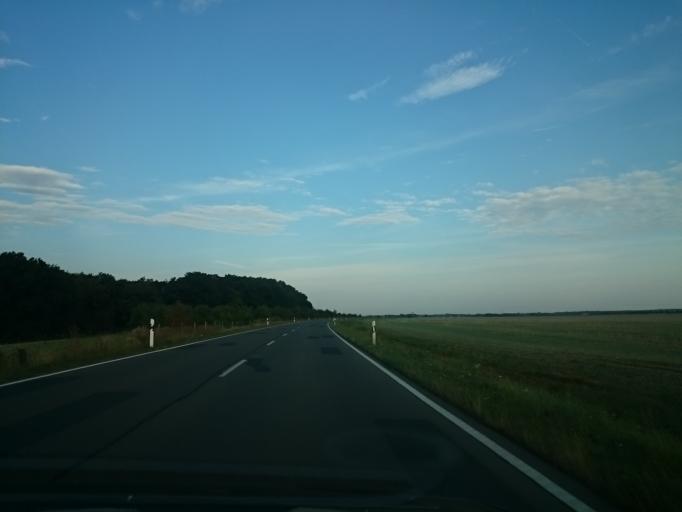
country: DE
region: Mecklenburg-Vorpommern
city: Gross Kiesow
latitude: 53.9369
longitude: 13.4371
